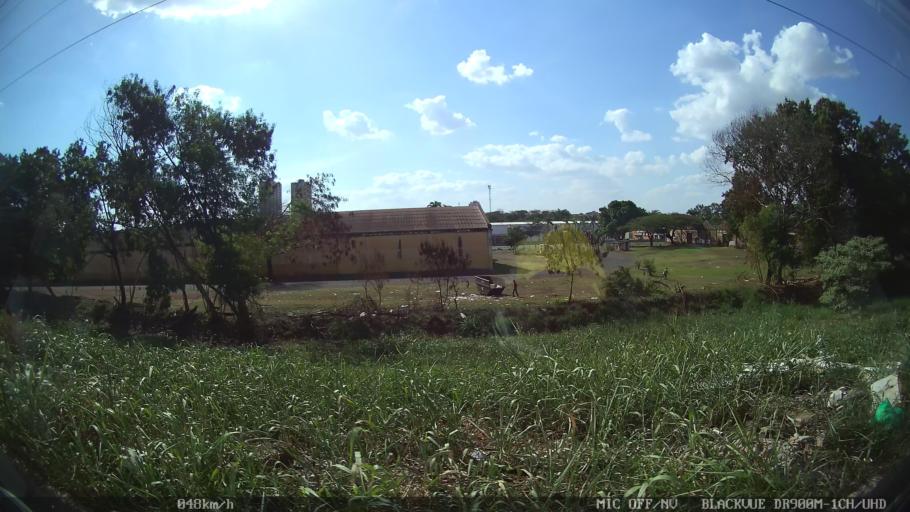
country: BR
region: Sao Paulo
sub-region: Ribeirao Preto
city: Ribeirao Preto
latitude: -21.1797
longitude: -47.8282
